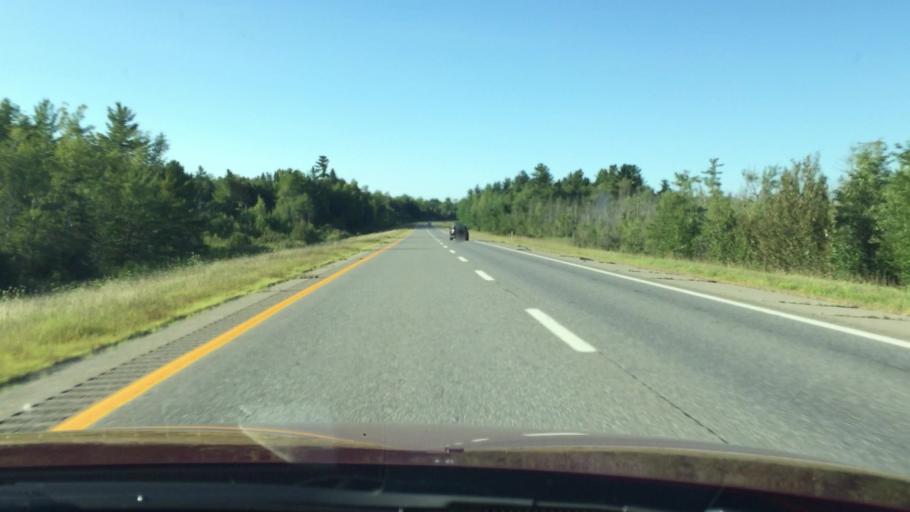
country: US
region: Maine
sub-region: Penobscot County
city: Lincoln
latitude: 45.4445
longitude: -68.5901
